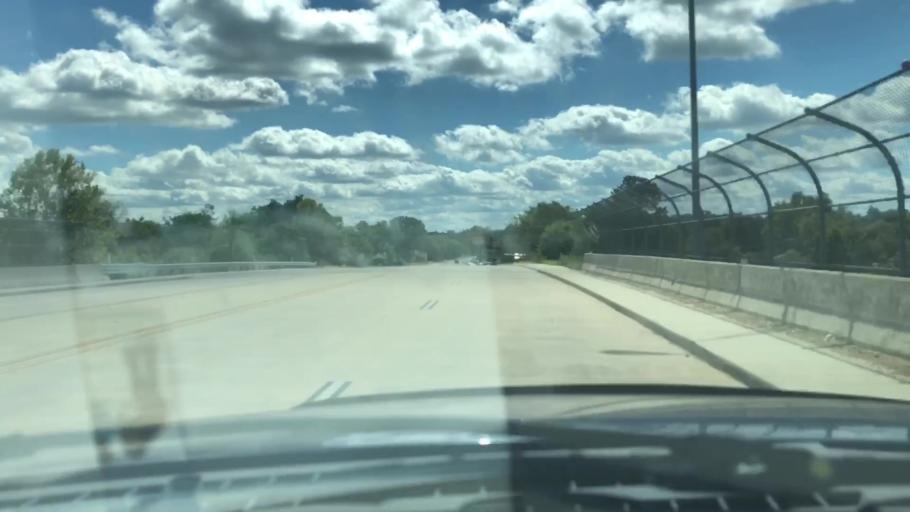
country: US
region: Texas
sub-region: Bowie County
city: Texarkana
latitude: 33.4136
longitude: -94.0611
